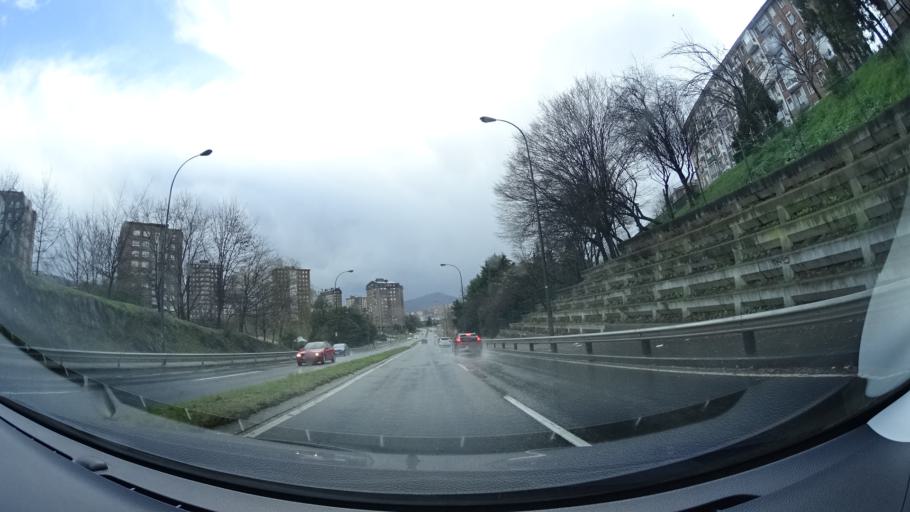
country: ES
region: Basque Country
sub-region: Bizkaia
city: Santutxu
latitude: 43.2534
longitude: -2.9090
